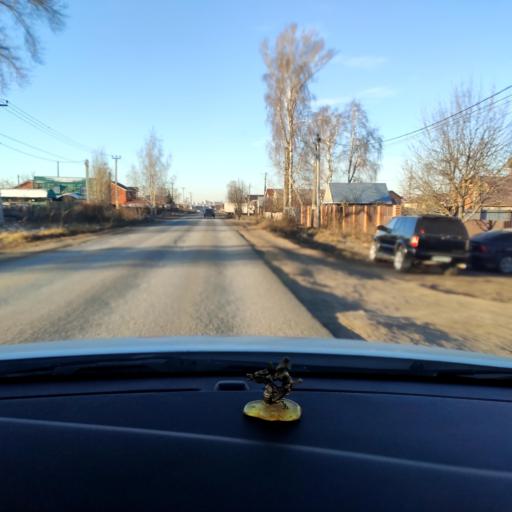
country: RU
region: Tatarstan
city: Stolbishchi
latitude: 55.7388
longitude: 49.3012
